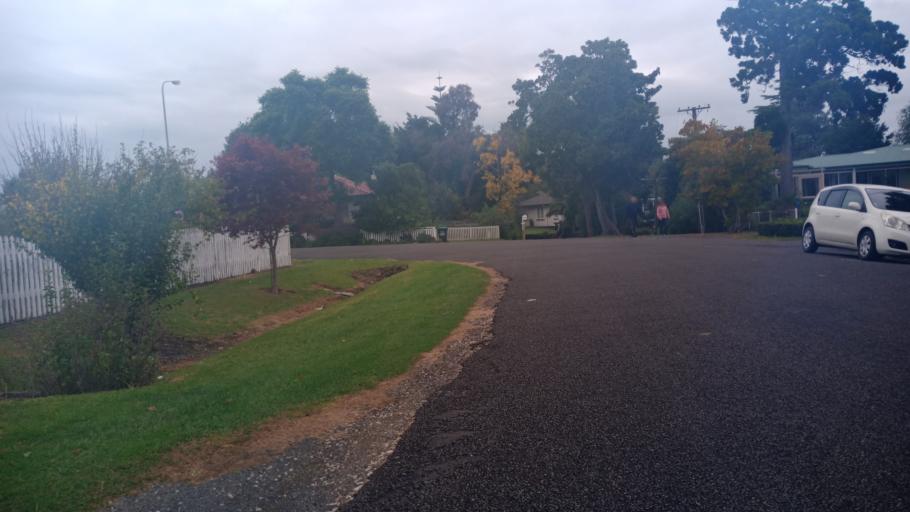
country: NZ
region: Gisborne
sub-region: Gisborne District
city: Gisborne
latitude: -38.6654
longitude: 178.0342
